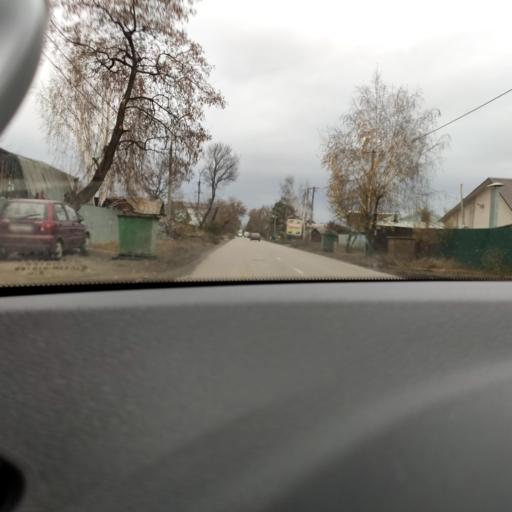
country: RU
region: Samara
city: Smyshlyayevka
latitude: 53.2390
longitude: 50.3297
